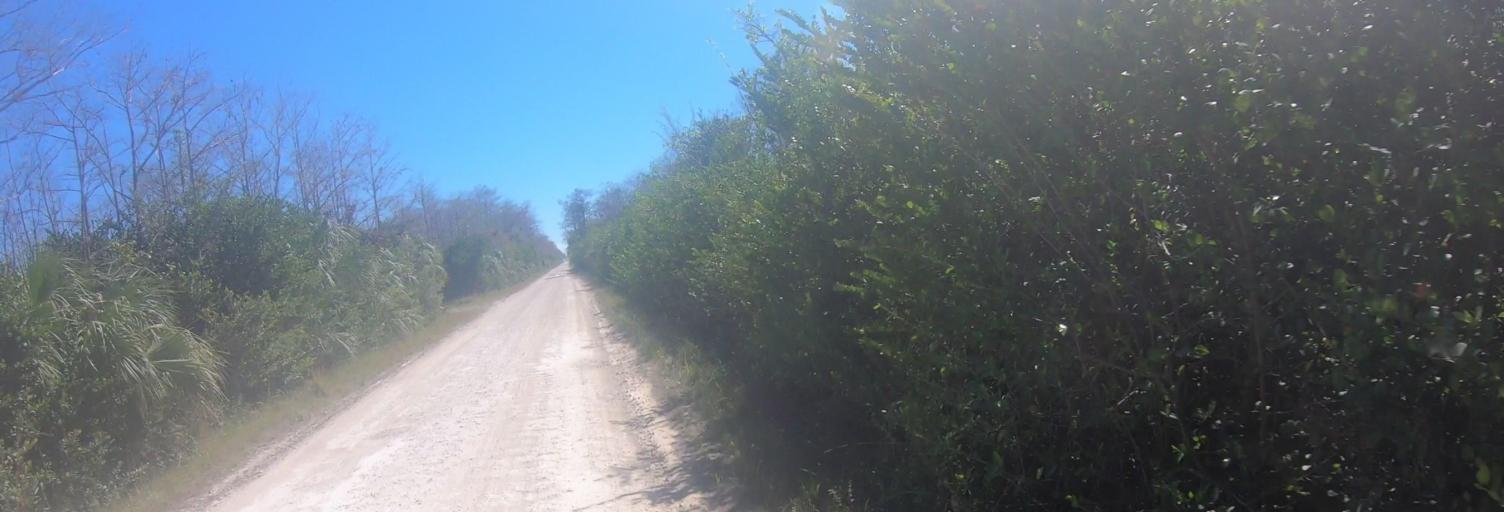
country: US
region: Florida
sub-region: Miami-Dade County
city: The Hammocks
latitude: 25.7596
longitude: -80.9938
